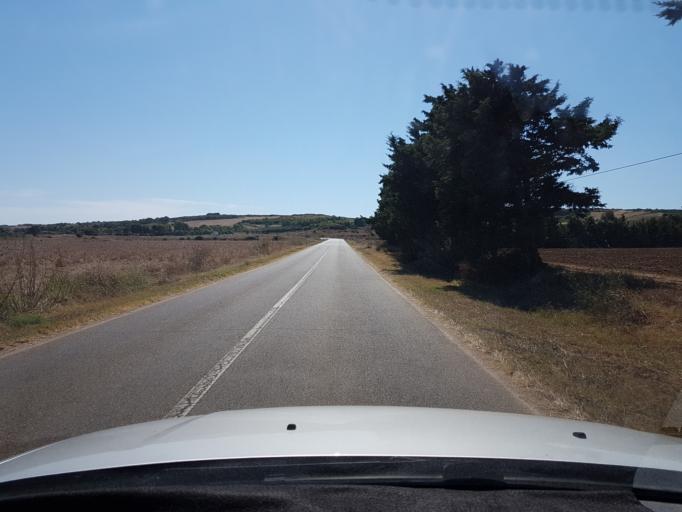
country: IT
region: Sardinia
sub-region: Provincia di Oristano
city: Cabras
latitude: 39.9115
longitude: 8.4418
